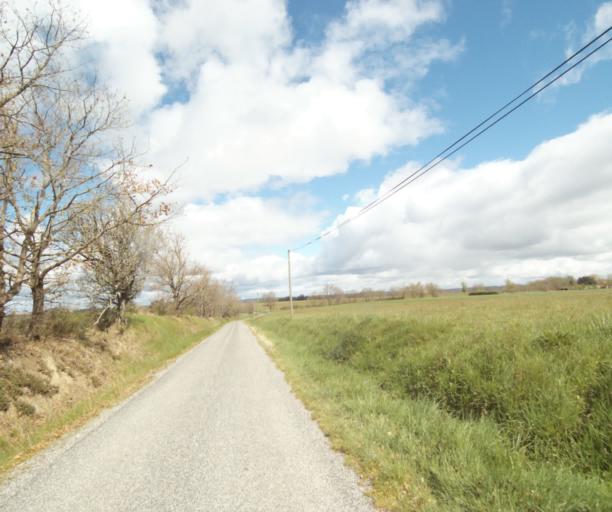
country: FR
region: Midi-Pyrenees
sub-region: Departement de l'Ariege
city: Saverdun
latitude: 43.2089
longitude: 1.5828
